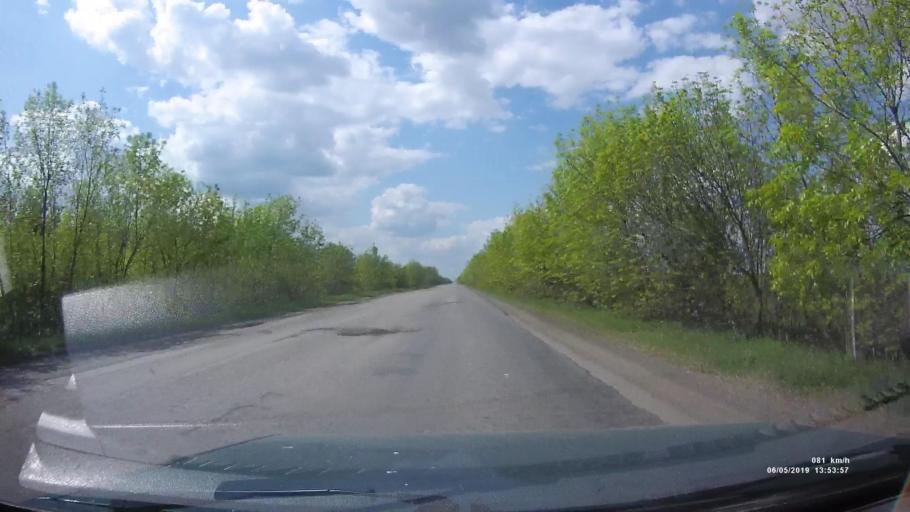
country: RU
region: Rostov
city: Melikhovskaya
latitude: 47.6715
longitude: 40.4544
